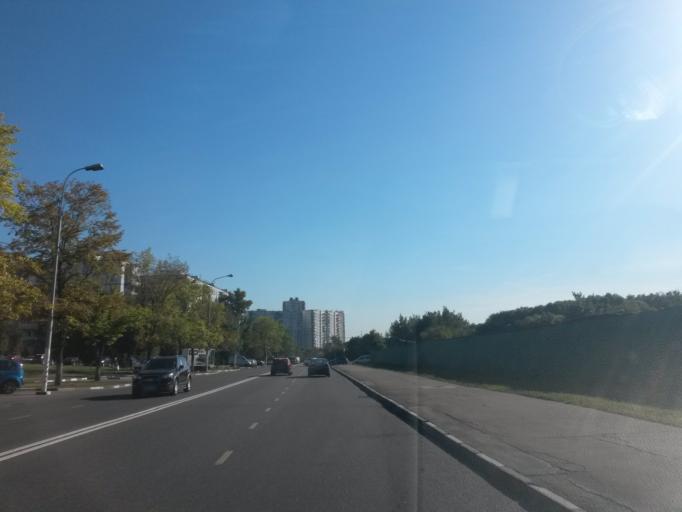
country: RU
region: Moscow
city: Yasenevo
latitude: 55.6066
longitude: 37.5120
